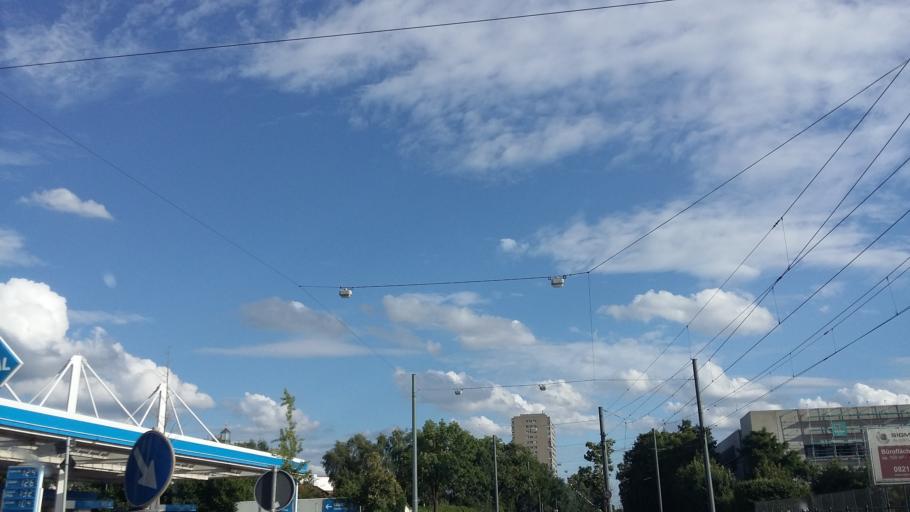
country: DE
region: Bavaria
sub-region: Swabia
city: Augsburg
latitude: 48.3467
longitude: 10.9048
